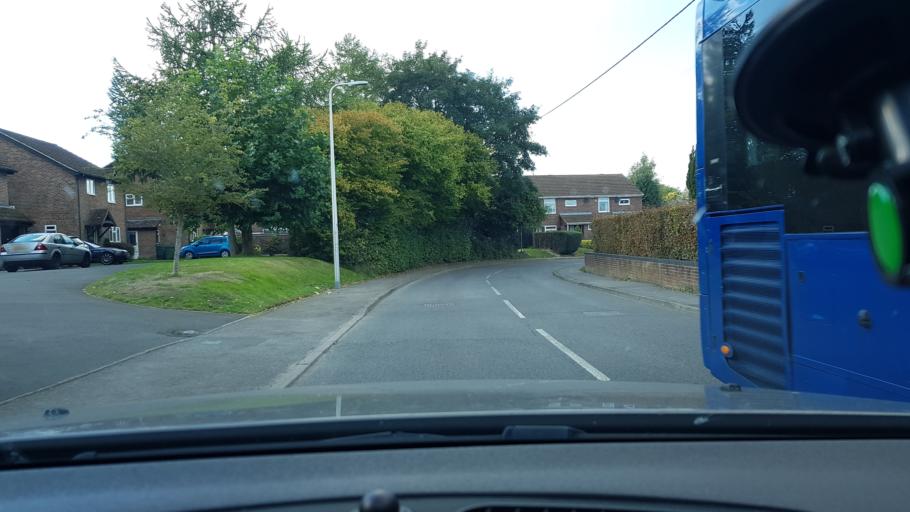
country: GB
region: England
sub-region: West Berkshire
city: Hungerford
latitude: 51.4062
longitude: -1.5167
